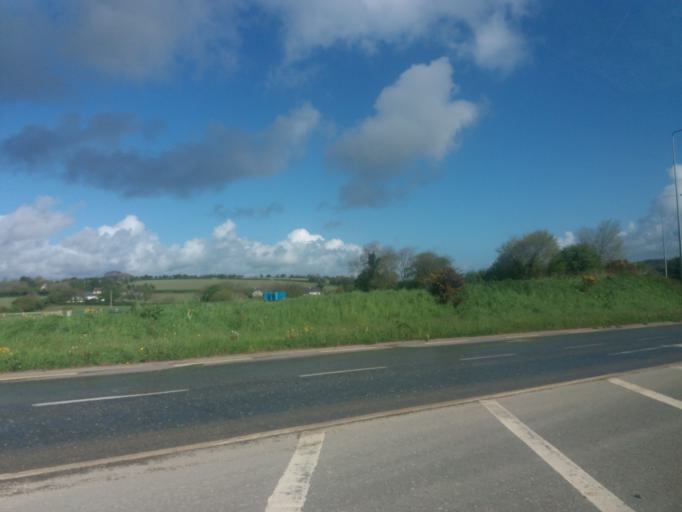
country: IE
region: Leinster
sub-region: Loch Garman
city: Enniscorthy
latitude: 52.5428
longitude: -6.5508
